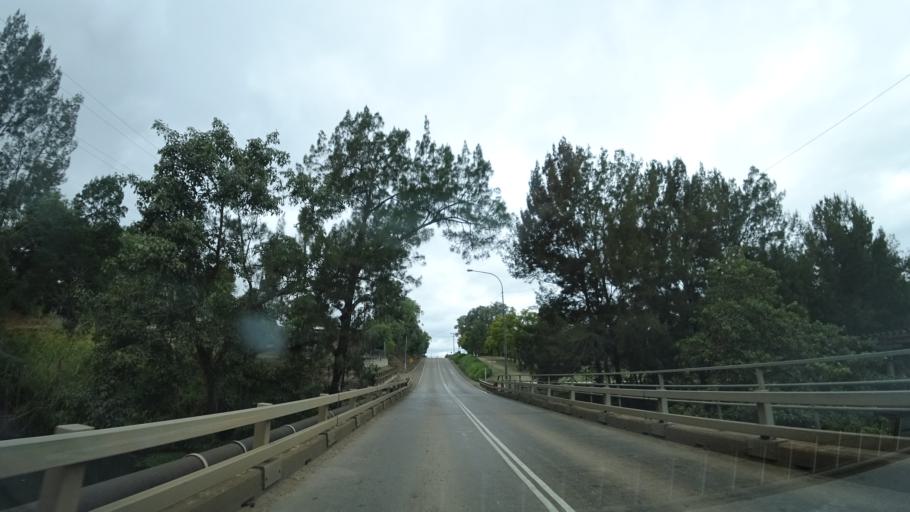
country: AU
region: Queensland
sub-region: Tablelands
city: Mareeba
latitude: -16.9862
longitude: 145.4193
